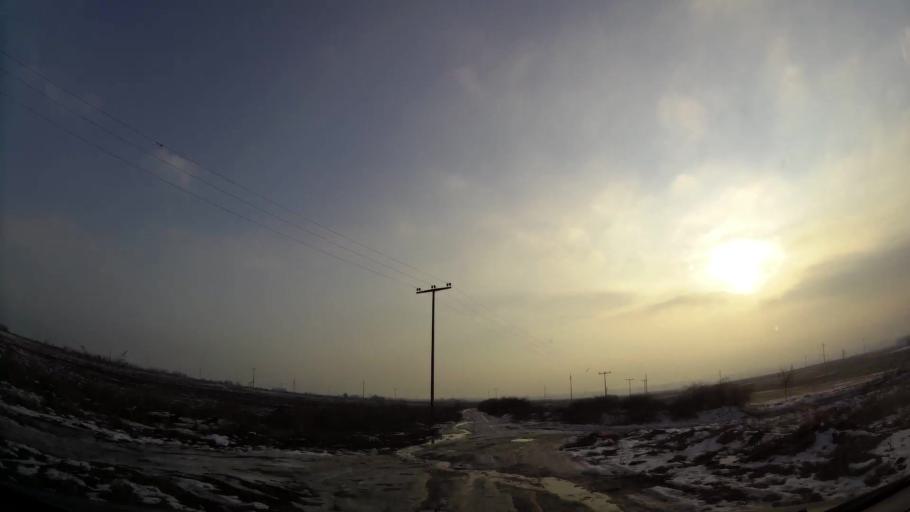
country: MK
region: Aracinovo
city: Arachinovo
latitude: 42.0194
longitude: 21.5676
